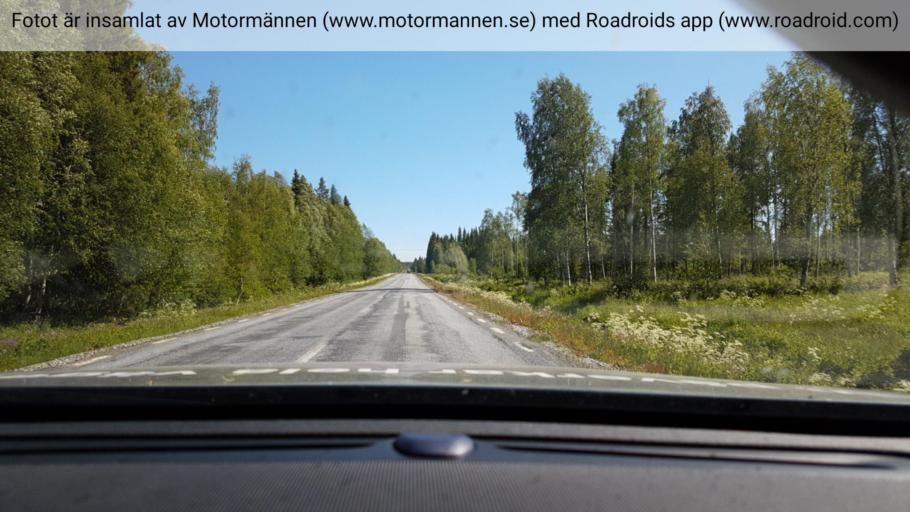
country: SE
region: Vaesterbotten
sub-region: Vilhelmina Kommun
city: Sjoberg
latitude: 64.7214
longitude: 16.2318
